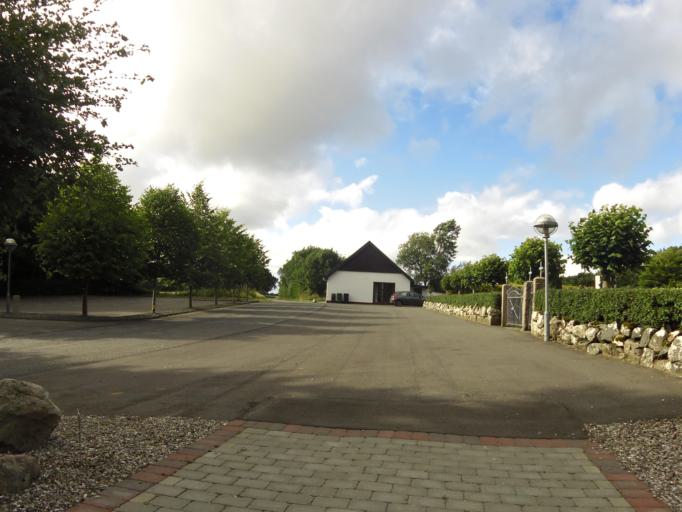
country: DK
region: South Denmark
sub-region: Tonder Kommune
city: Toftlund
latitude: 55.1281
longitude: 9.0784
